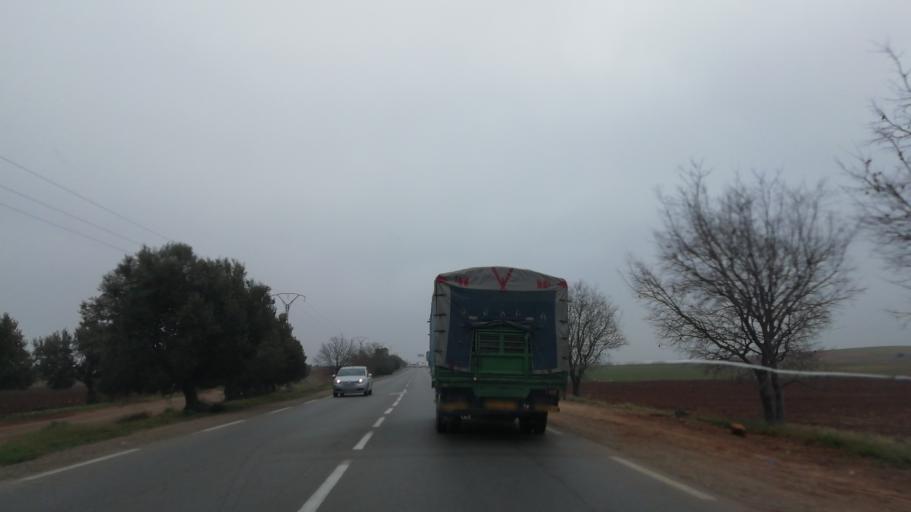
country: DZ
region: Mascara
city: Mascara
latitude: 35.3178
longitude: 0.3716
